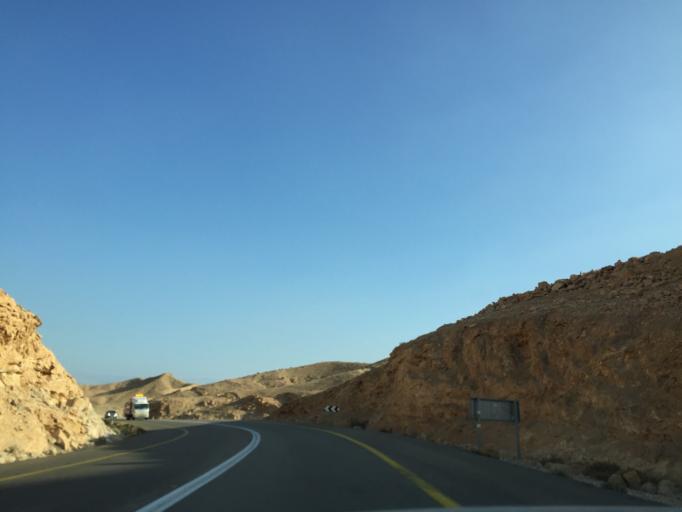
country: IL
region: Southern District
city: `En Boqeq
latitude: 31.1936
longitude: 35.2769
